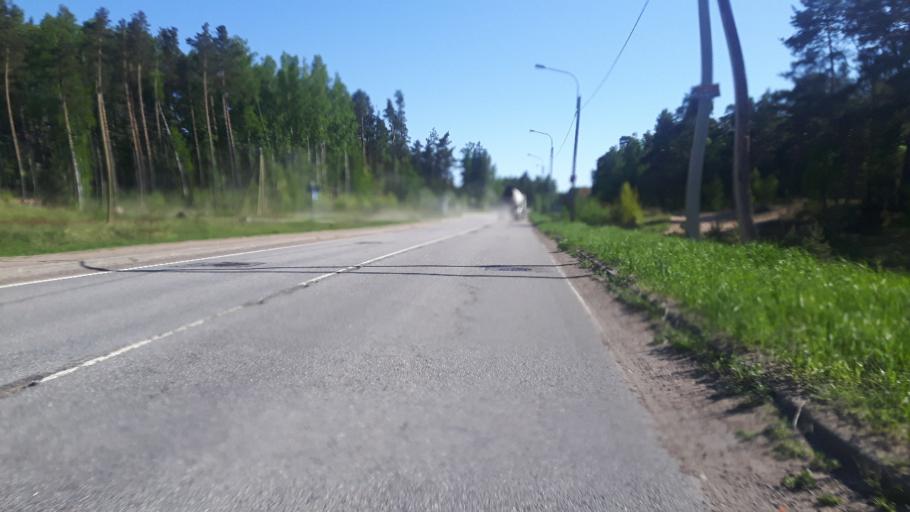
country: RU
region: Leningrad
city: Sosnovyy Bor
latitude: 60.2002
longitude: 29.0070
